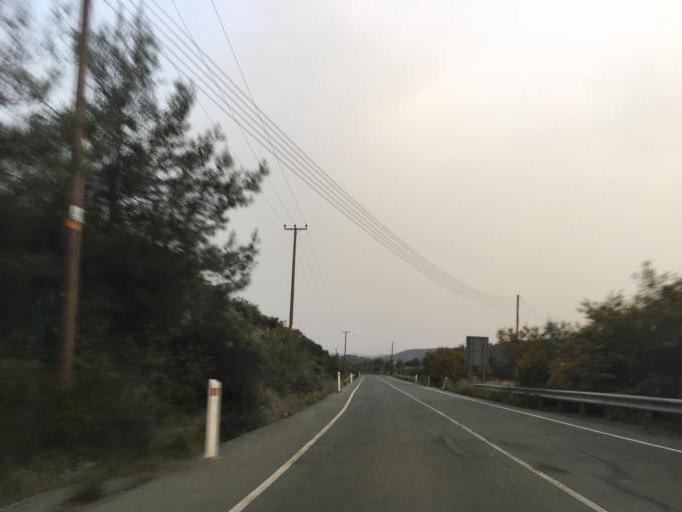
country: CY
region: Limassol
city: Parekklisha
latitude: 34.8062
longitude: 33.1447
